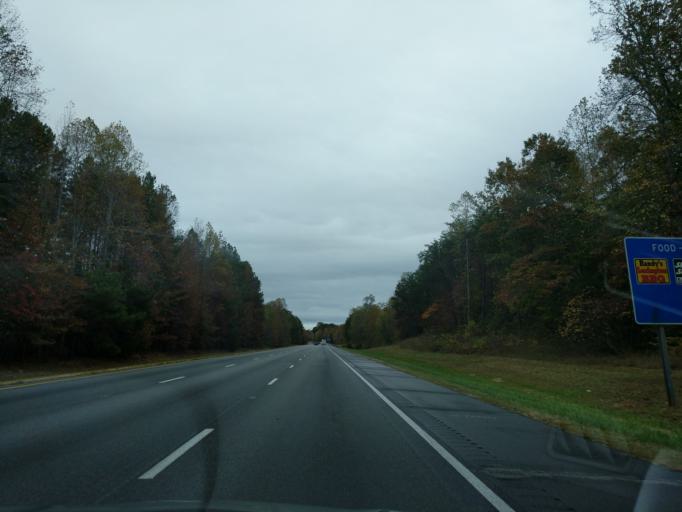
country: US
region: North Carolina
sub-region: Davidson County
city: Lexington
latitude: 35.8021
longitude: -80.1962
